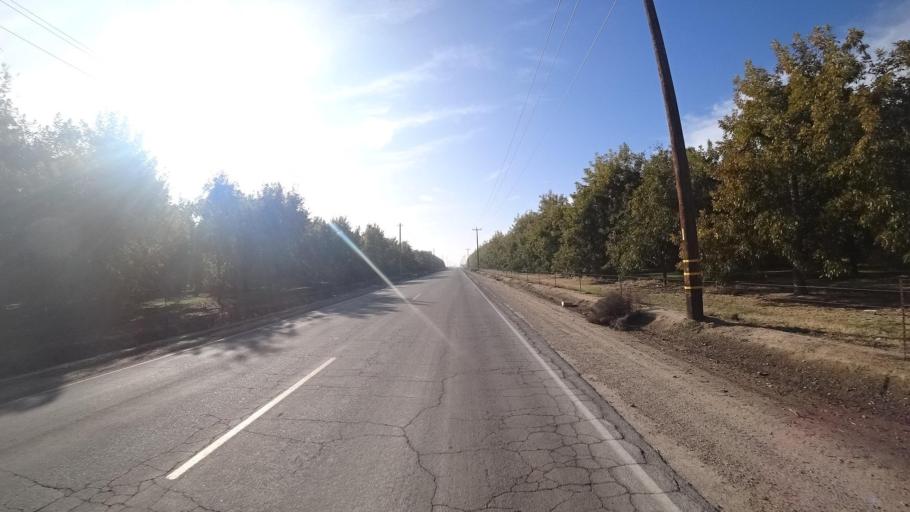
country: US
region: California
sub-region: Kern County
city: McFarland
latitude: 35.6200
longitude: -119.2044
